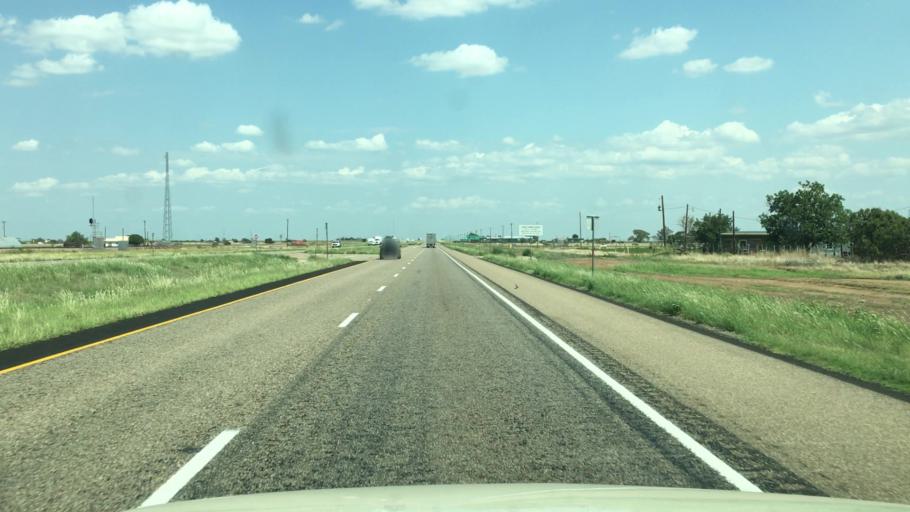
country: US
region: Texas
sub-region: Armstrong County
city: Claude
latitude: 35.0342
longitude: -101.1903
